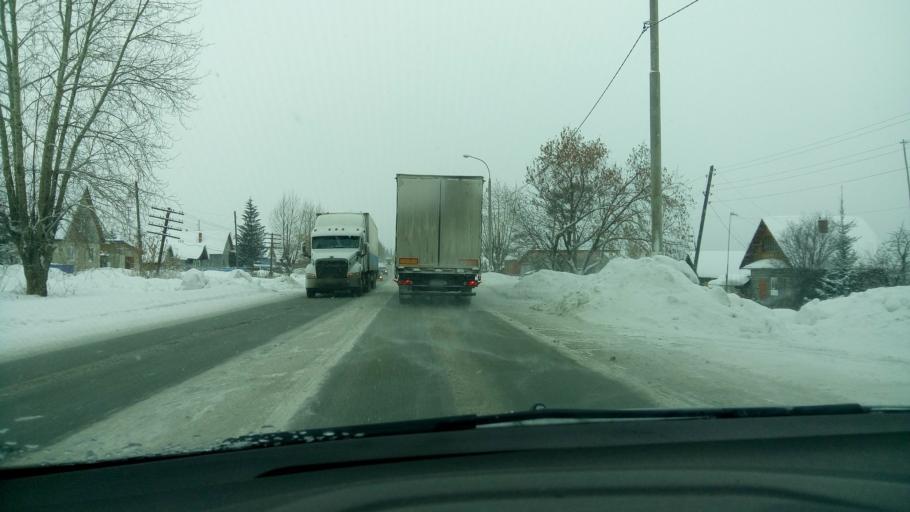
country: RU
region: Sverdlovsk
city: Beloyarskiy
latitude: 56.7572
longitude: 61.3647
